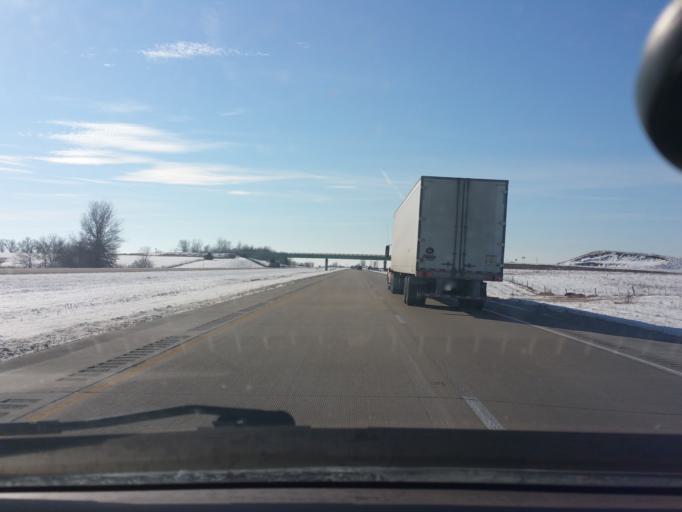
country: US
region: Iowa
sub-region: Decatur County
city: Leon
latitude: 40.8055
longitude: -93.8302
